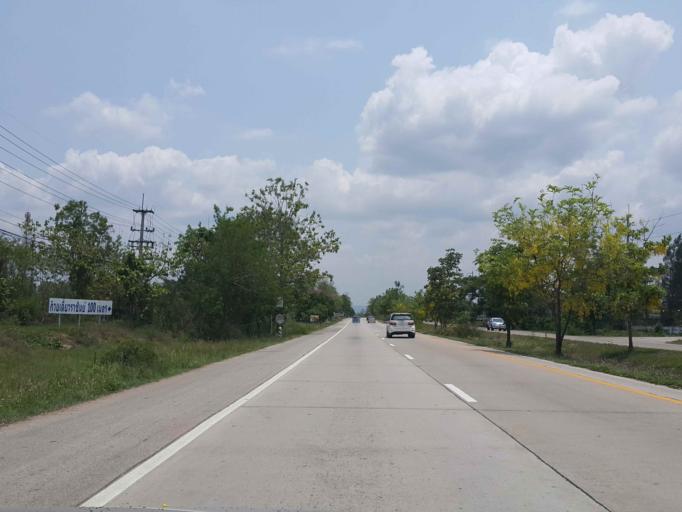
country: TH
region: Lampang
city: Hang Chat
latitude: 18.2994
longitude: 99.4098
